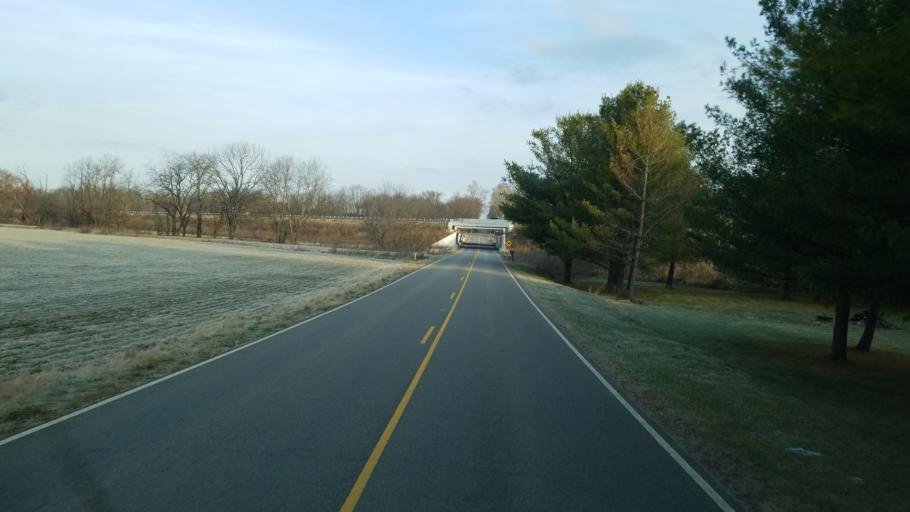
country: US
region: Ohio
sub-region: Ross County
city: Chillicothe
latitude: 39.2623
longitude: -82.8702
